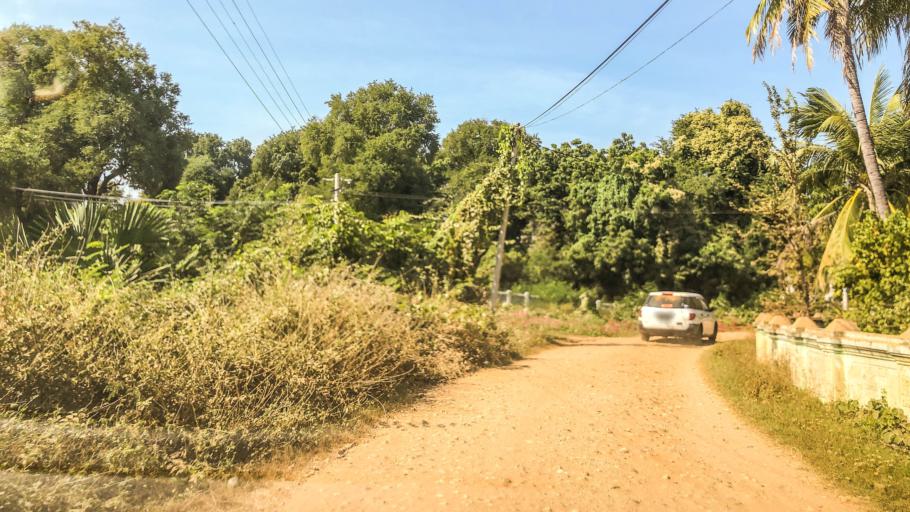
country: MM
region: Magway
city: Magway
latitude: 19.9752
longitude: 95.0356
